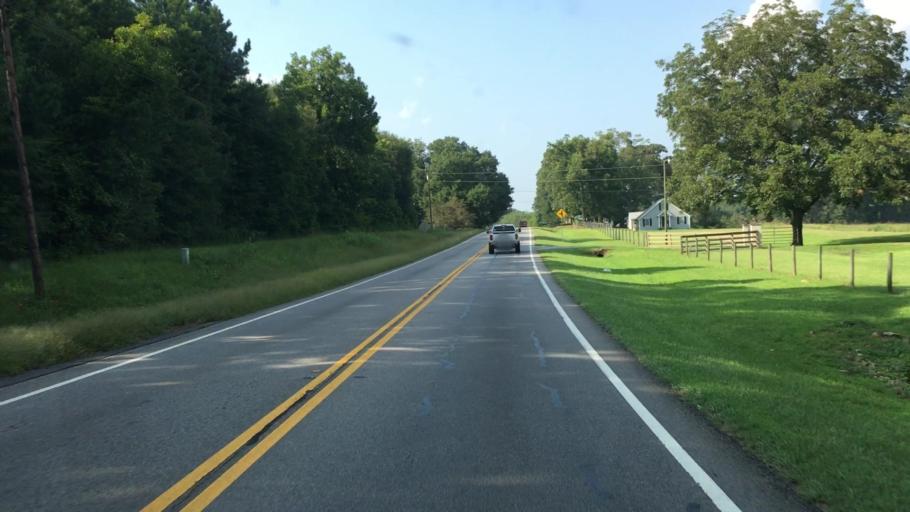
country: US
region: Georgia
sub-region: Walton County
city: Monroe
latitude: 33.8766
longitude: -83.7210
